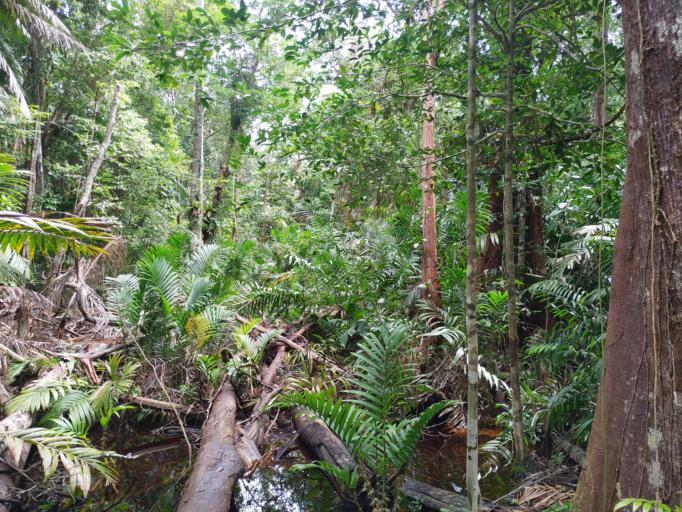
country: MY
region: Sarawak
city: Kuching
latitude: 1.7127
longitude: 110.4447
